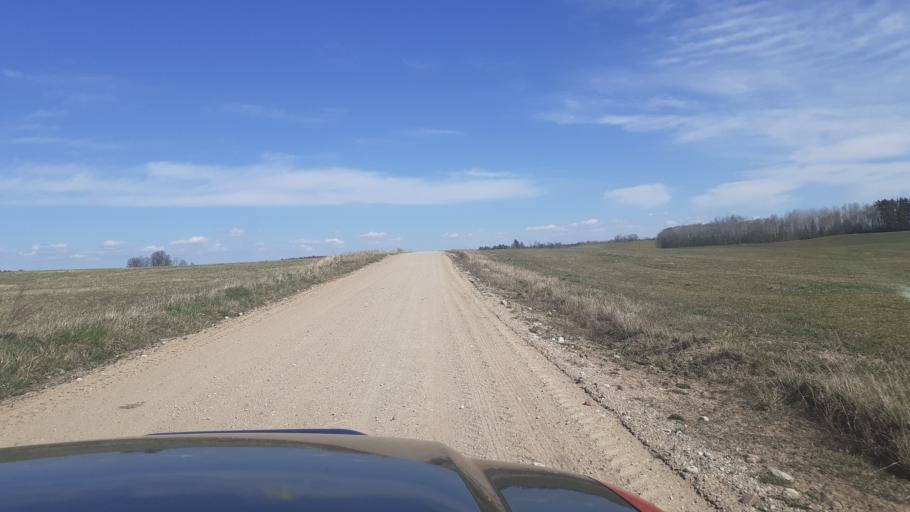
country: LV
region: Kuldigas Rajons
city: Kuldiga
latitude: 56.8492
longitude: 21.9933
